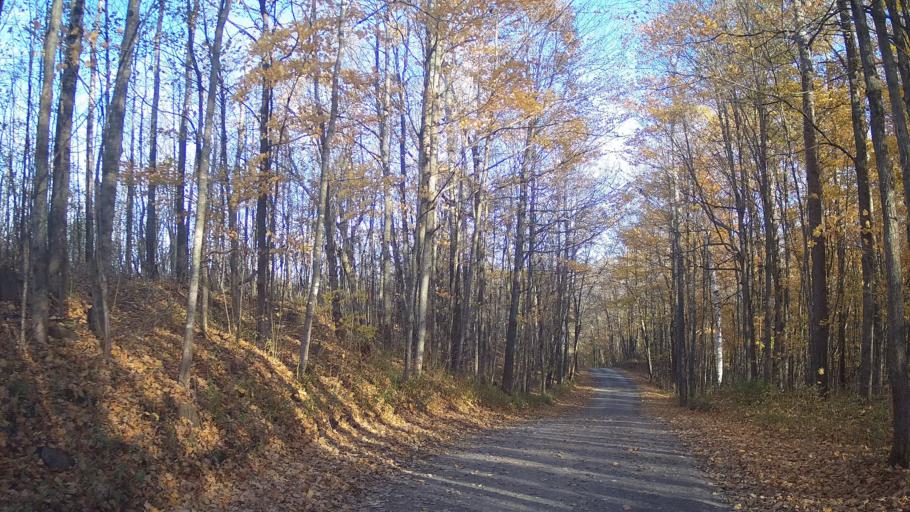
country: CA
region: Ontario
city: Perth
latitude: 44.7450
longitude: -76.4051
